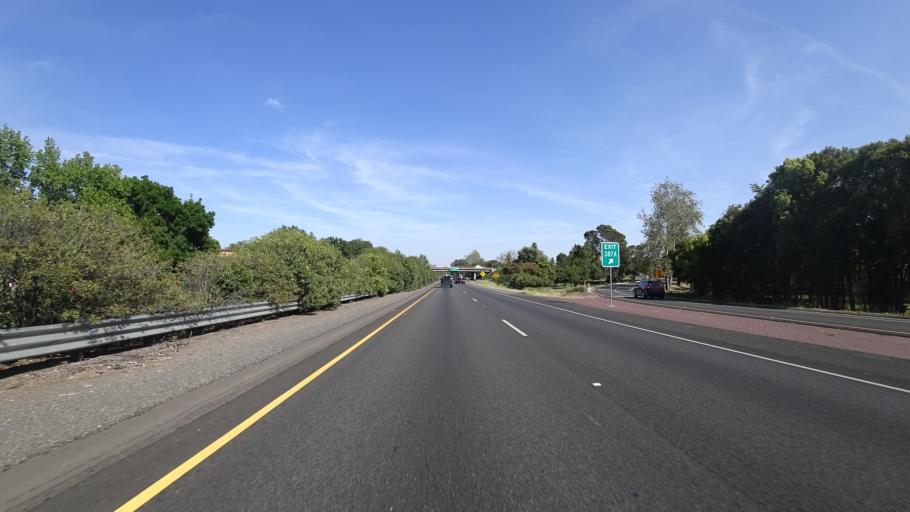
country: US
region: California
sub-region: Butte County
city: Chico
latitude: 39.7553
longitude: -121.8472
